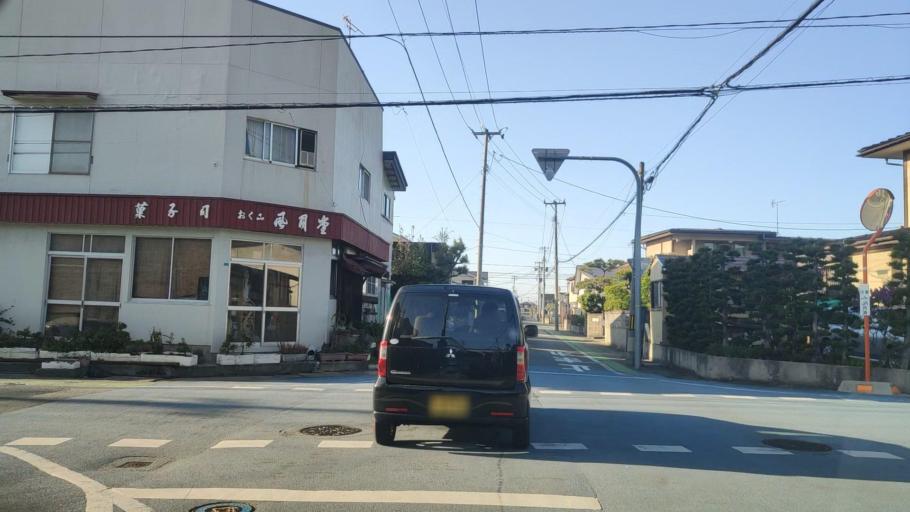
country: JP
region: Yamagata
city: Tendo
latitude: 38.3624
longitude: 140.3843
